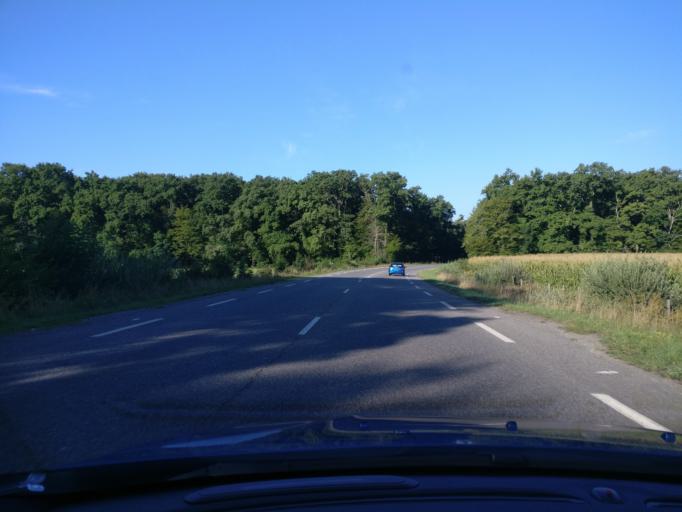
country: FR
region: Rhone-Alpes
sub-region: Departement de l'Ain
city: Ferney-Voltaire
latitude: 46.2493
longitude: 6.1089
